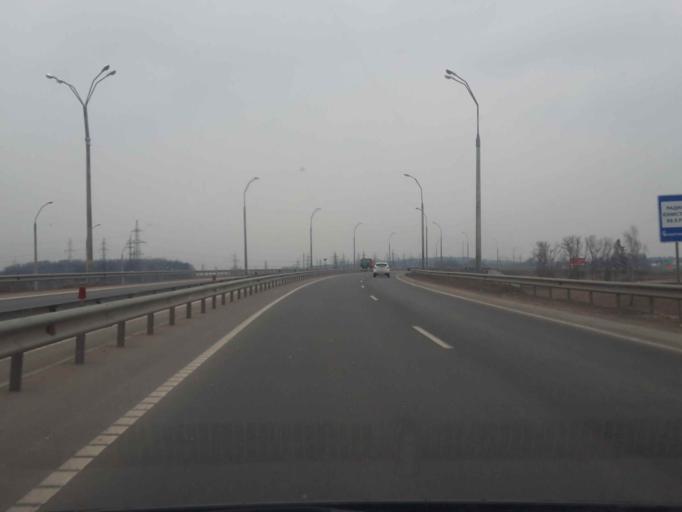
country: BY
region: Minsk
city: Bal'shavik
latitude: 53.9825
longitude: 27.5326
